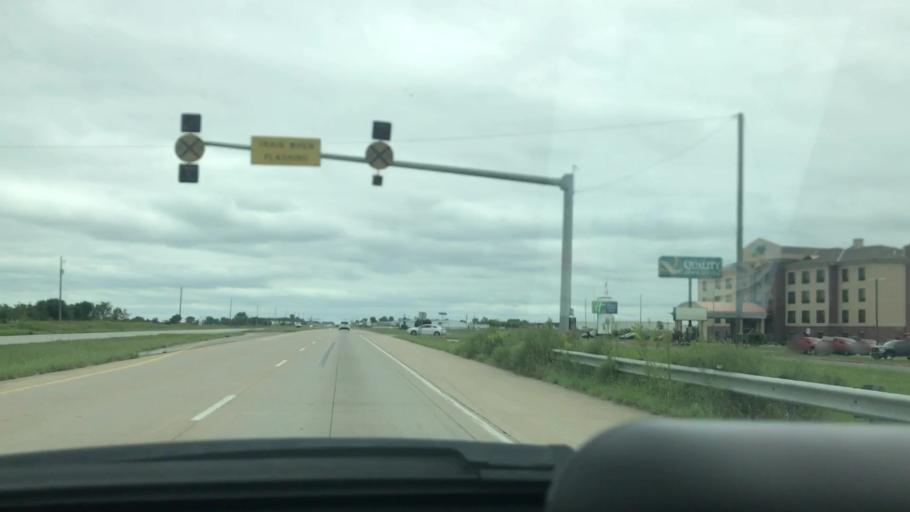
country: US
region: Oklahoma
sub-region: Mayes County
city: Chouteau
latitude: 36.2307
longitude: -95.3394
